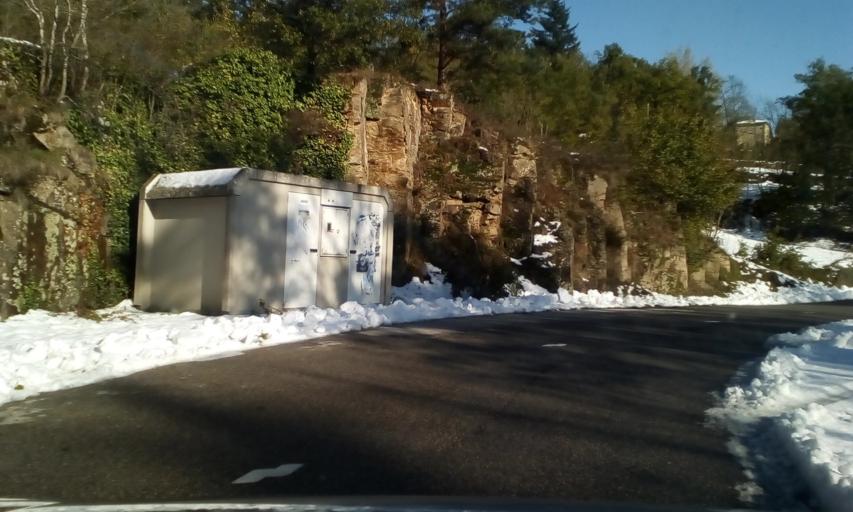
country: FR
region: Rhone-Alpes
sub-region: Departement de l'Ardeche
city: Saint-Felicien
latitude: 45.0826
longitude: 4.5990
